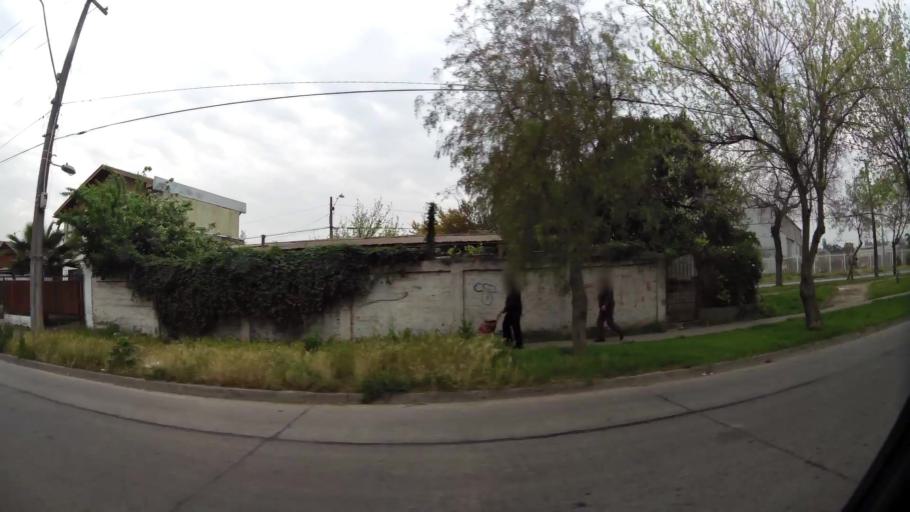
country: CL
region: Santiago Metropolitan
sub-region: Provincia de Santiago
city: Lo Prado
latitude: -33.4874
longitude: -70.7156
